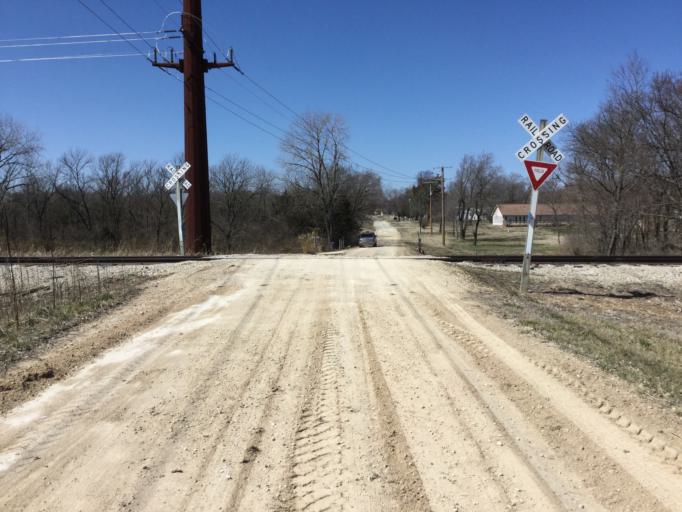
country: US
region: Kansas
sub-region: Allen County
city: Humboldt
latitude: 37.8057
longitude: -95.4284
